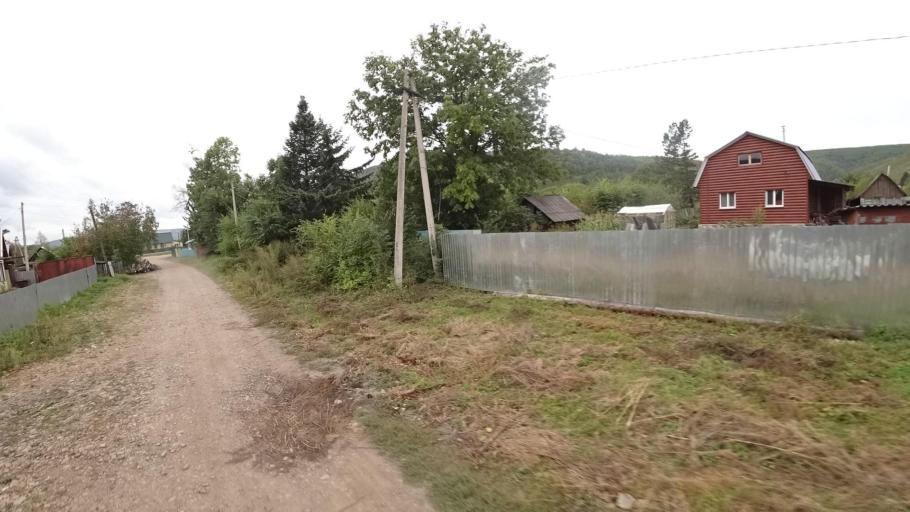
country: RU
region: Jewish Autonomous Oblast
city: Khingansk
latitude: 49.0089
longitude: 131.0480
